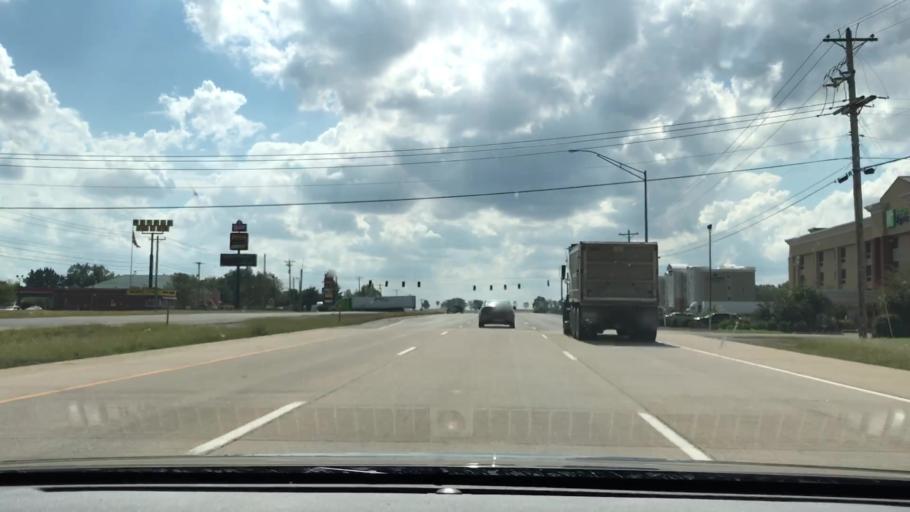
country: US
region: Kentucky
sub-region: Christian County
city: Oak Grove
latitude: 36.6948
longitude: -87.4533
